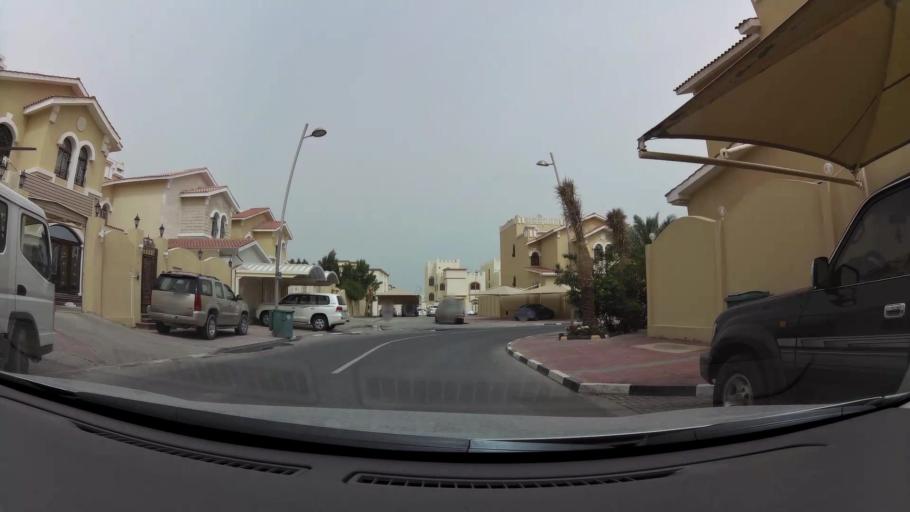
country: QA
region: Baladiyat ad Dawhah
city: Doha
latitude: 25.2284
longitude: 51.5383
